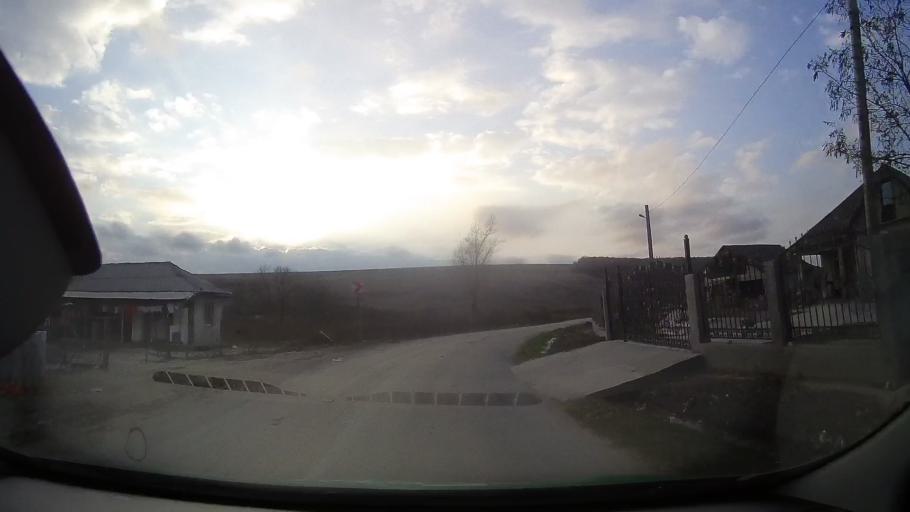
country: RO
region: Constanta
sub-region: Comuna Dobromir
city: Dobromir
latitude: 44.0216
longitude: 27.8723
